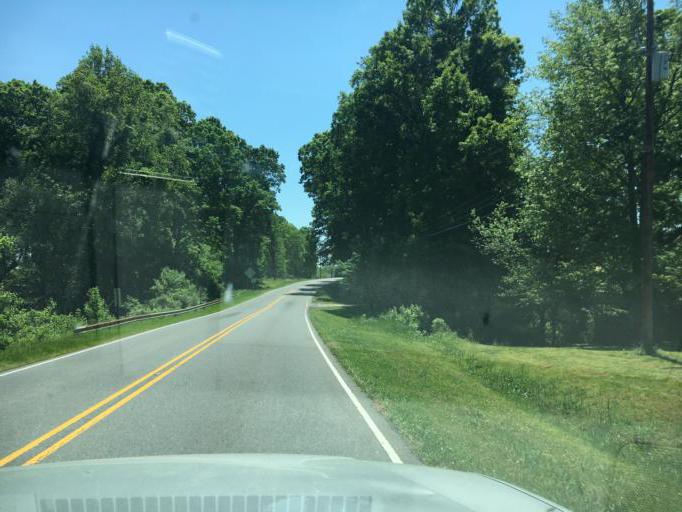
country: US
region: South Carolina
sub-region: Cherokee County
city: Blacksburg
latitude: 35.2017
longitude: -81.5628
